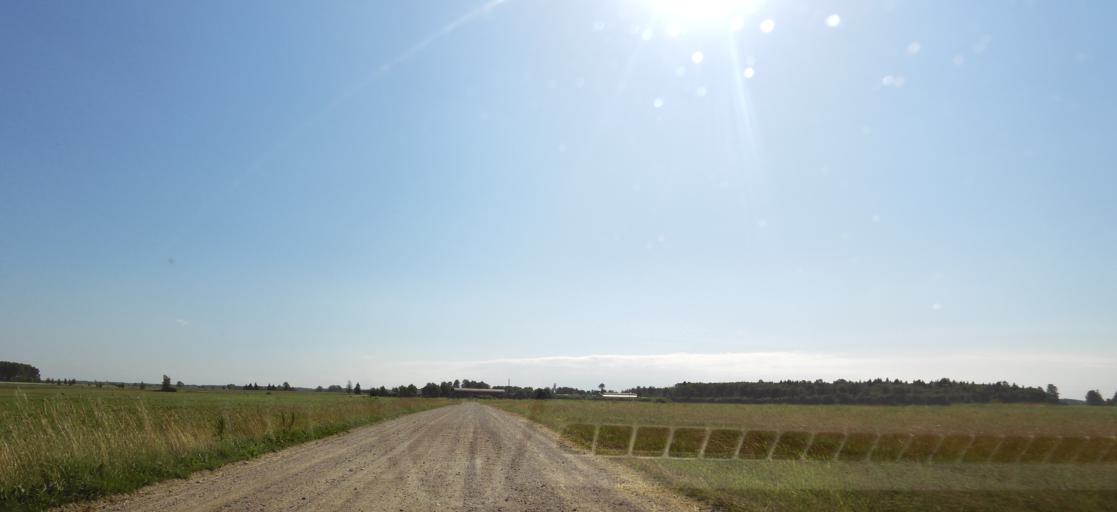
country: LT
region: Panevezys
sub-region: Birzai
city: Birzai
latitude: 56.2450
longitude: 24.8645
